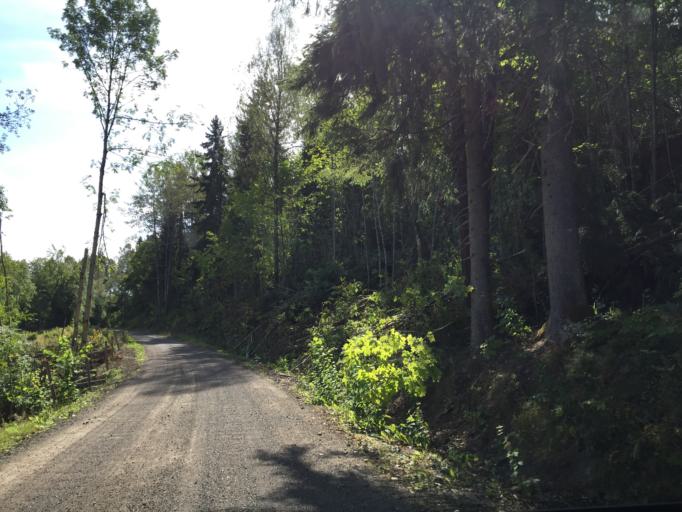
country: NO
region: Vestfold
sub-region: Hof
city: Hof
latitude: 59.4520
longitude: 10.1514
